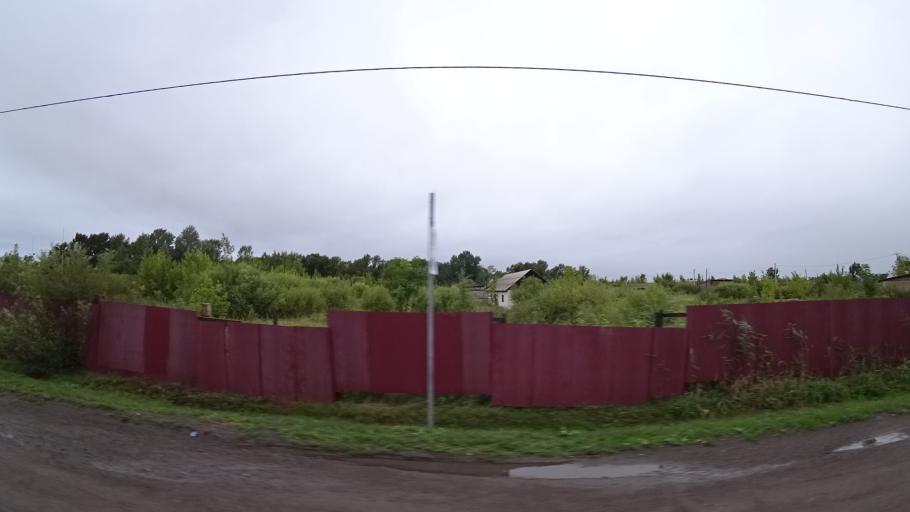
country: RU
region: Primorskiy
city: Chernigovka
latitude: 44.3303
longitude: 132.5755
